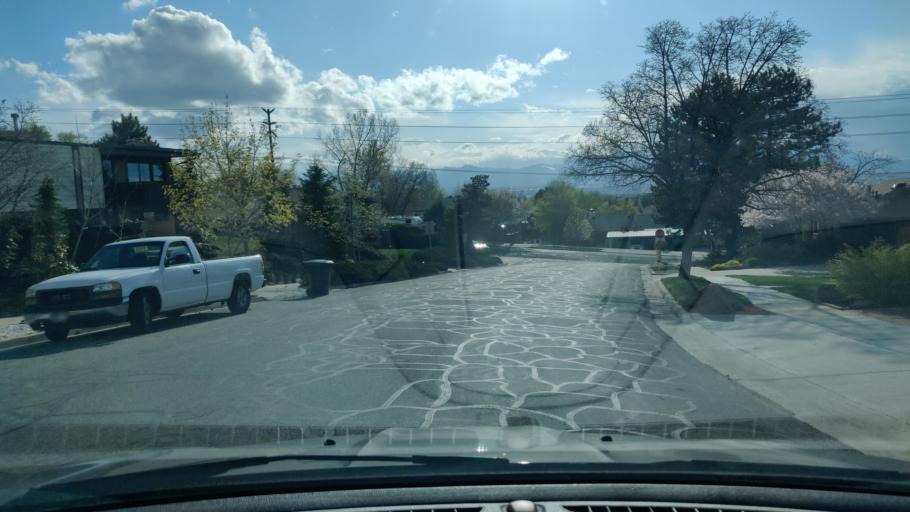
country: US
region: Utah
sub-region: Salt Lake County
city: Cottonwood Heights
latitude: 40.6185
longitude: -111.8239
